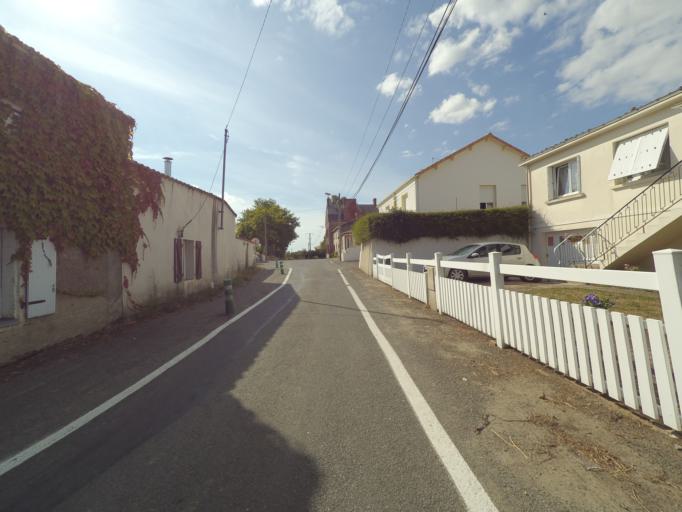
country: FR
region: Pays de la Loire
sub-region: Departement de la Loire-Atlantique
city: Vieillevigne
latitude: 46.9686
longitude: -1.4240
